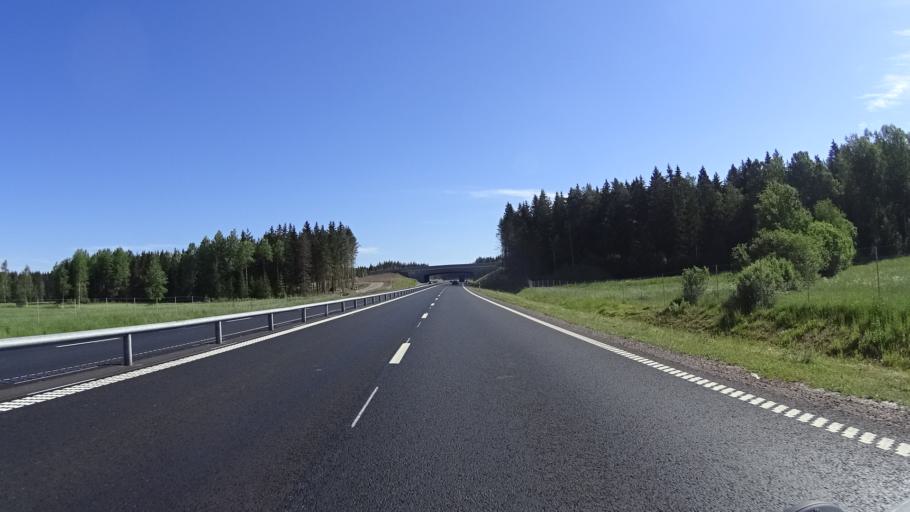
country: SE
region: Vaestra Goetaland
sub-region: Gullspangs Kommun
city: Hova
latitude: 58.8337
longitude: 14.1800
